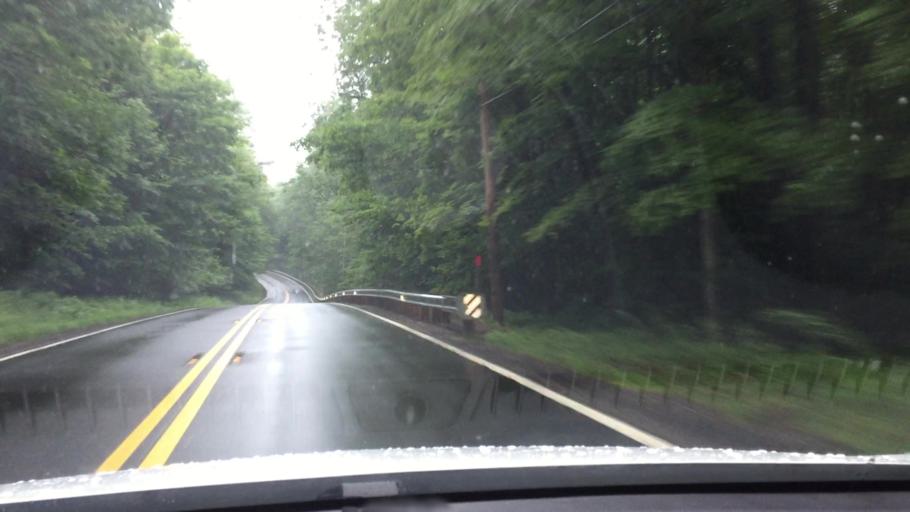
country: US
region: Massachusetts
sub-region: Berkshire County
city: Becket
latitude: 42.3454
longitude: -73.1176
